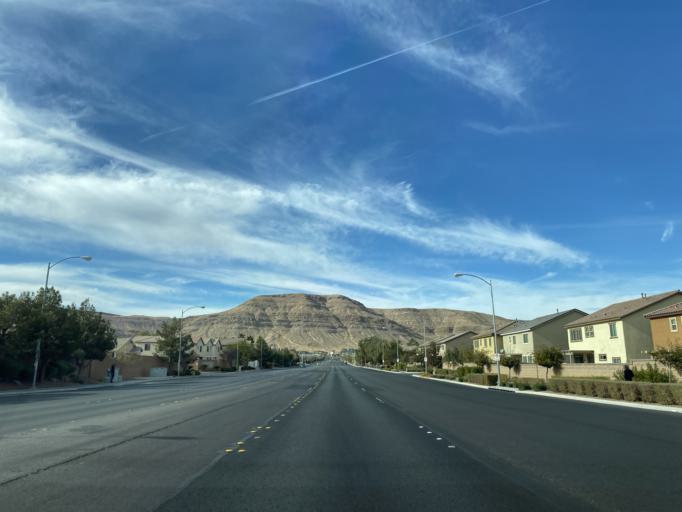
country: US
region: Nevada
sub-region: Clark County
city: Summerlin South
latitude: 36.0702
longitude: -115.3016
